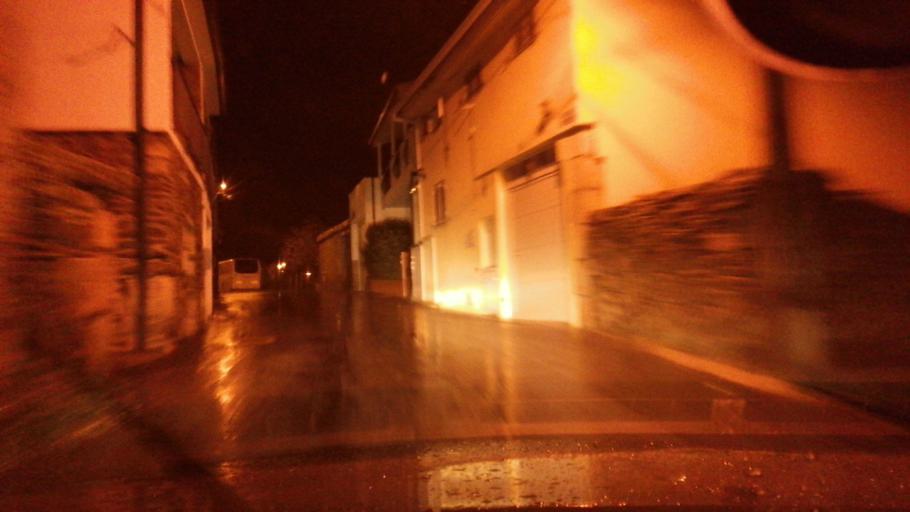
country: PT
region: Viseu
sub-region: Armamar
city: Armamar
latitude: 41.1128
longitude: -7.7156
